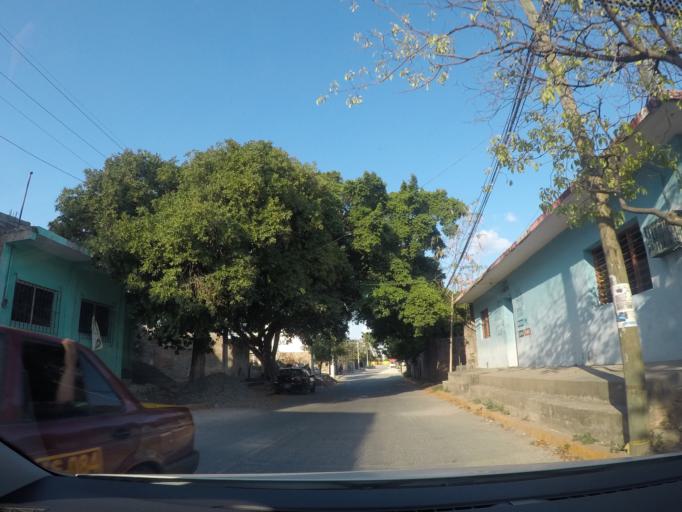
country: MX
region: Oaxaca
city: Juchitan de Zaragoza
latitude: 16.4336
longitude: -95.0270
